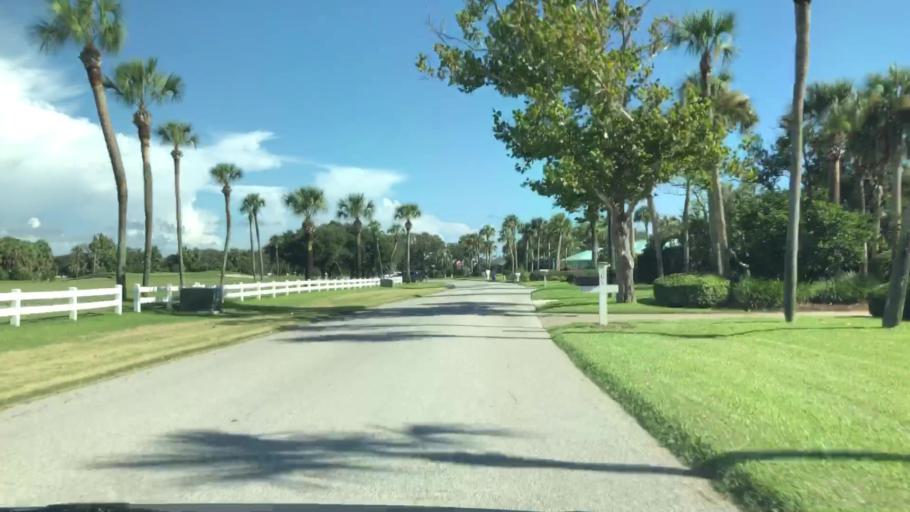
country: US
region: Florida
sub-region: Saint Johns County
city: Ponte Vedra Beach
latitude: 30.2368
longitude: -81.3805
